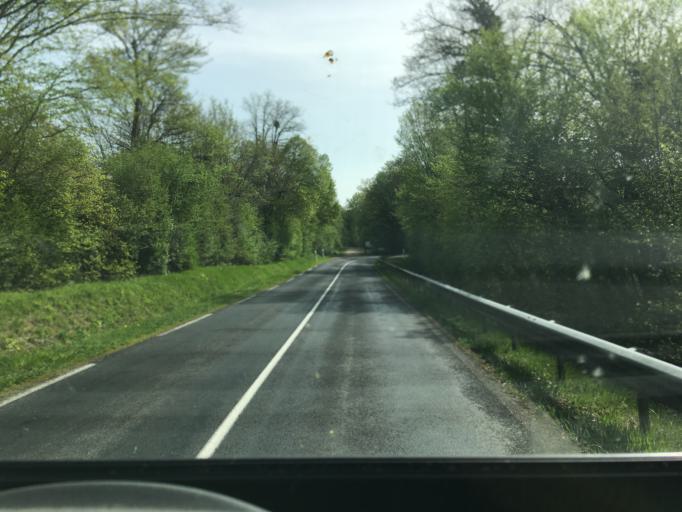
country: FR
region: Lorraine
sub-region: Departement de Meurthe-et-Moselle
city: Velaine-en-Haye
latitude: 48.6642
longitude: 6.0106
